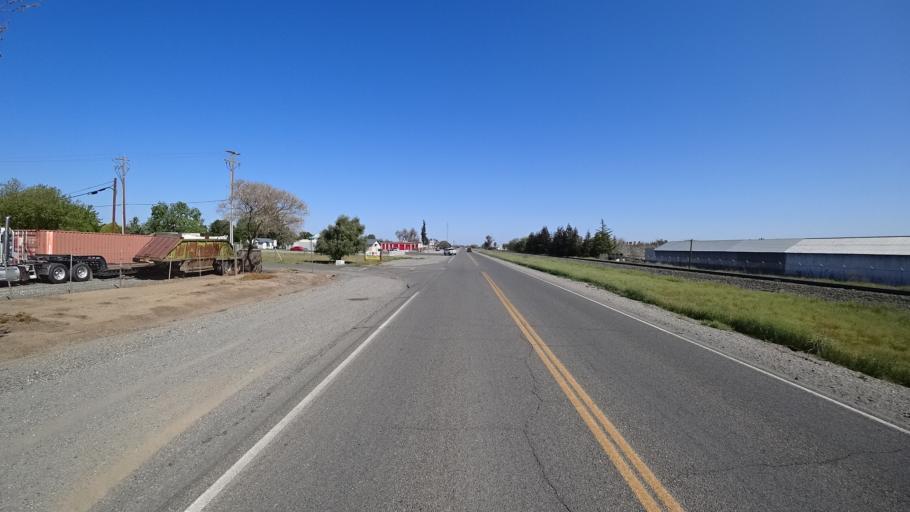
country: US
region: California
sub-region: Glenn County
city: Willows
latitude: 39.5331
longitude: -122.1935
